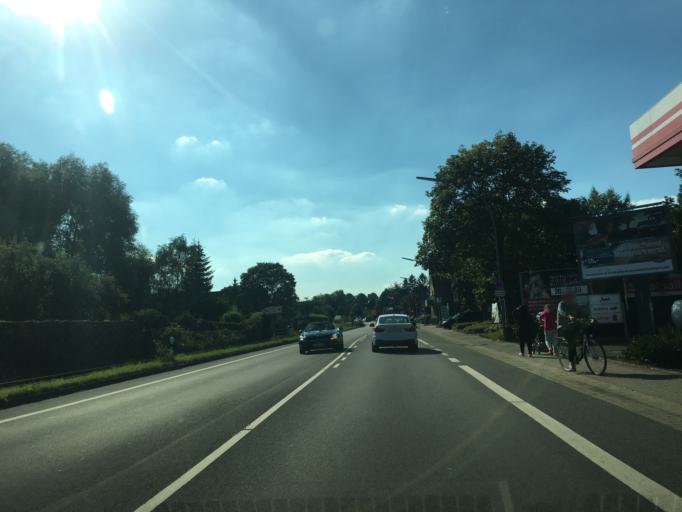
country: DE
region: North Rhine-Westphalia
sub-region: Regierungsbezirk Munster
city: Warendorf
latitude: 51.9498
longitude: 8.0014
